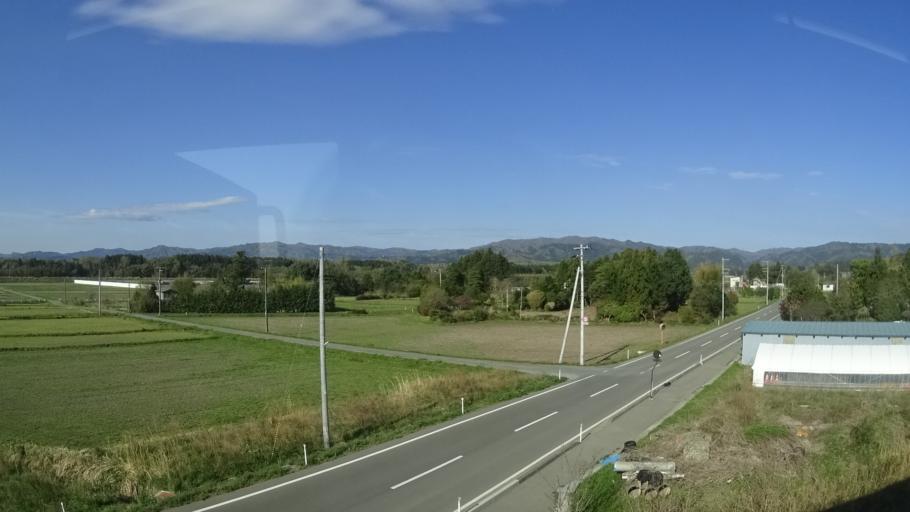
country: JP
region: Fukushima
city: Namie
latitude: 37.5028
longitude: 140.9791
